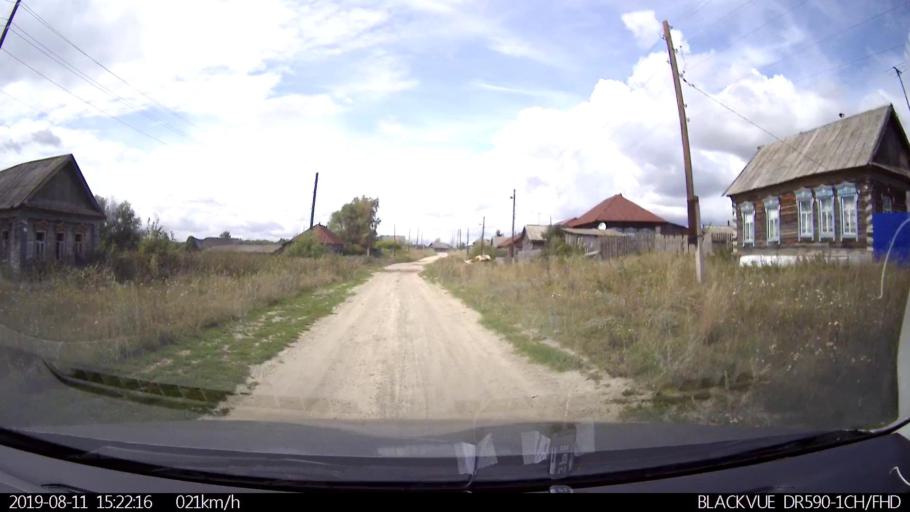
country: RU
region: Ulyanovsk
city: Ignatovka
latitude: 53.8459
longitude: 47.5816
